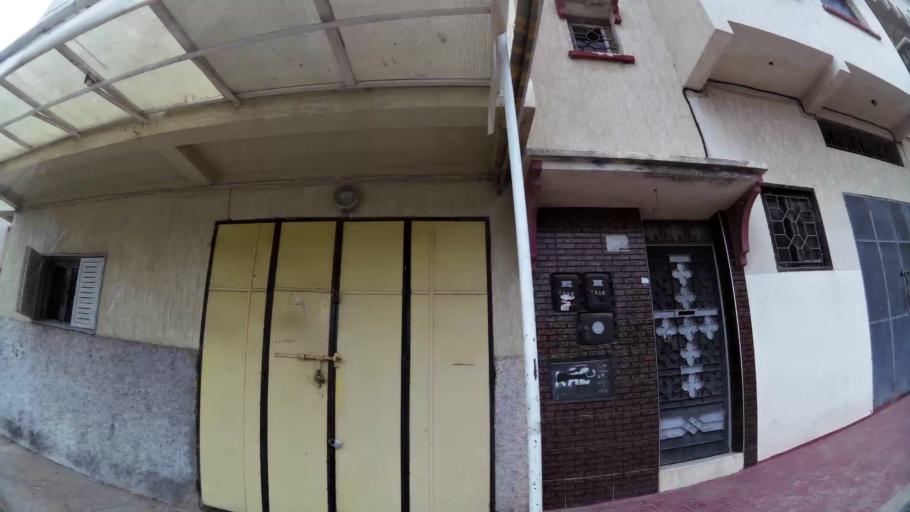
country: MA
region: Rabat-Sale-Zemmour-Zaer
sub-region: Rabat
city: Rabat
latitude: 33.9792
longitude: -6.8232
